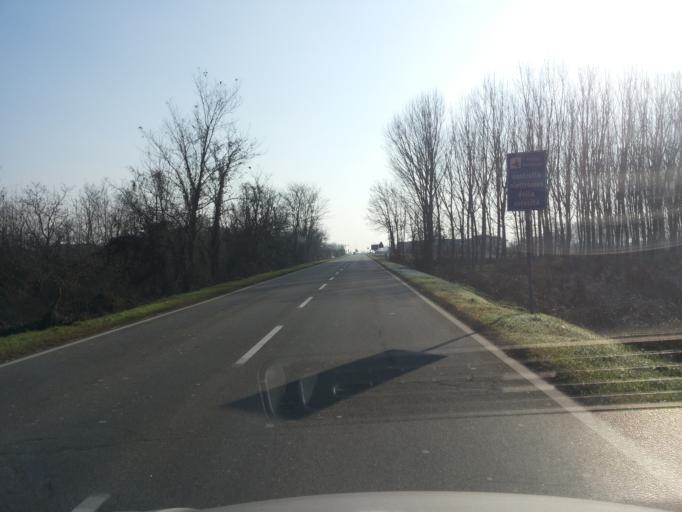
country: IT
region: Piedmont
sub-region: Provincia di Vercelli
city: Caresana
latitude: 45.2185
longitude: 8.5024
